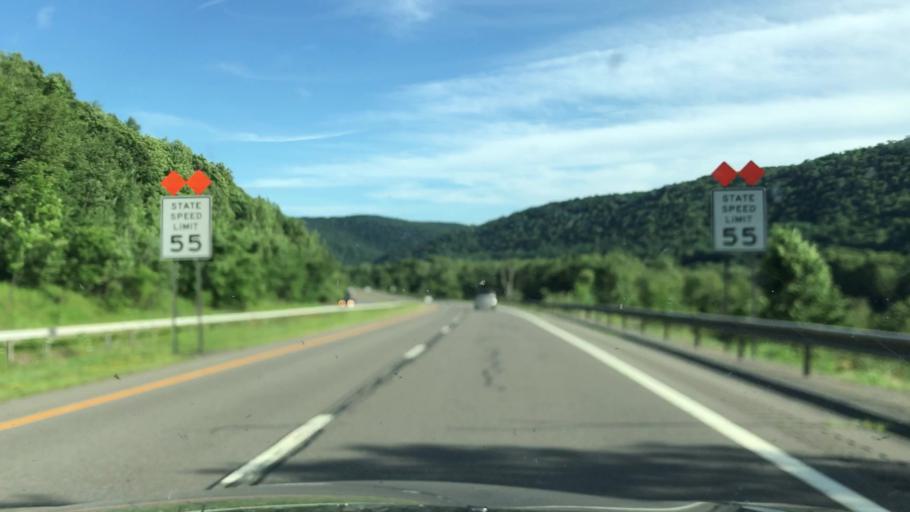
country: US
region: New York
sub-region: Broome County
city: Deposit
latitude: 42.0241
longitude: -75.4064
